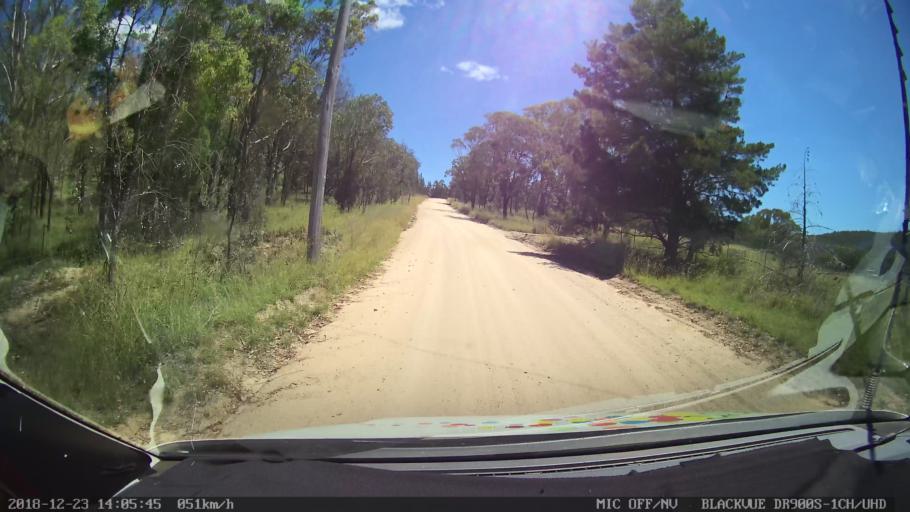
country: AU
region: New South Wales
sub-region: Tamworth Municipality
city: Manilla
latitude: -30.6261
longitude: 151.0785
